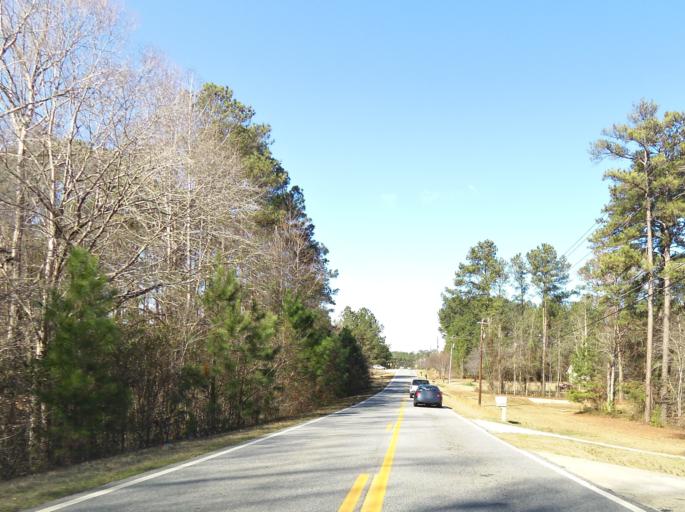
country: US
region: Georgia
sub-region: Bibb County
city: West Point
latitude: 32.8662
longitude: -83.7567
